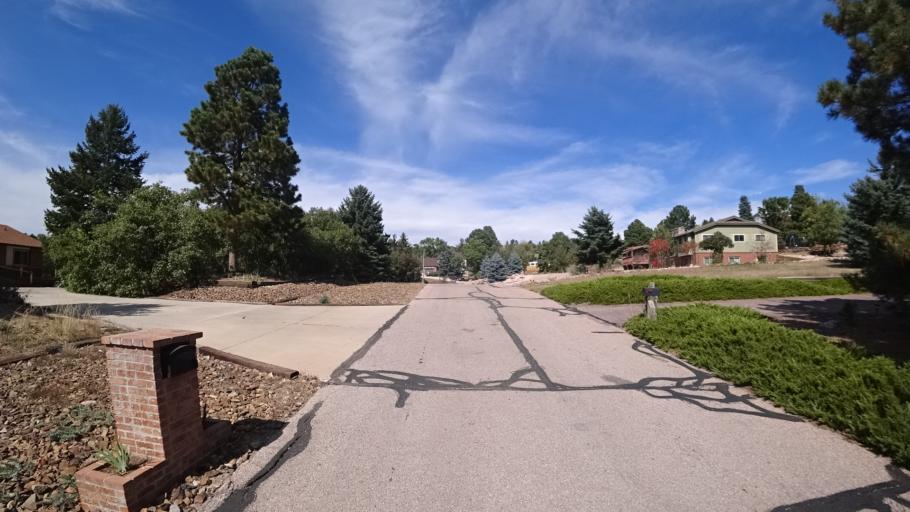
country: US
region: Colorado
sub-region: El Paso County
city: Cimarron Hills
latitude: 38.9089
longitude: -104.7596
